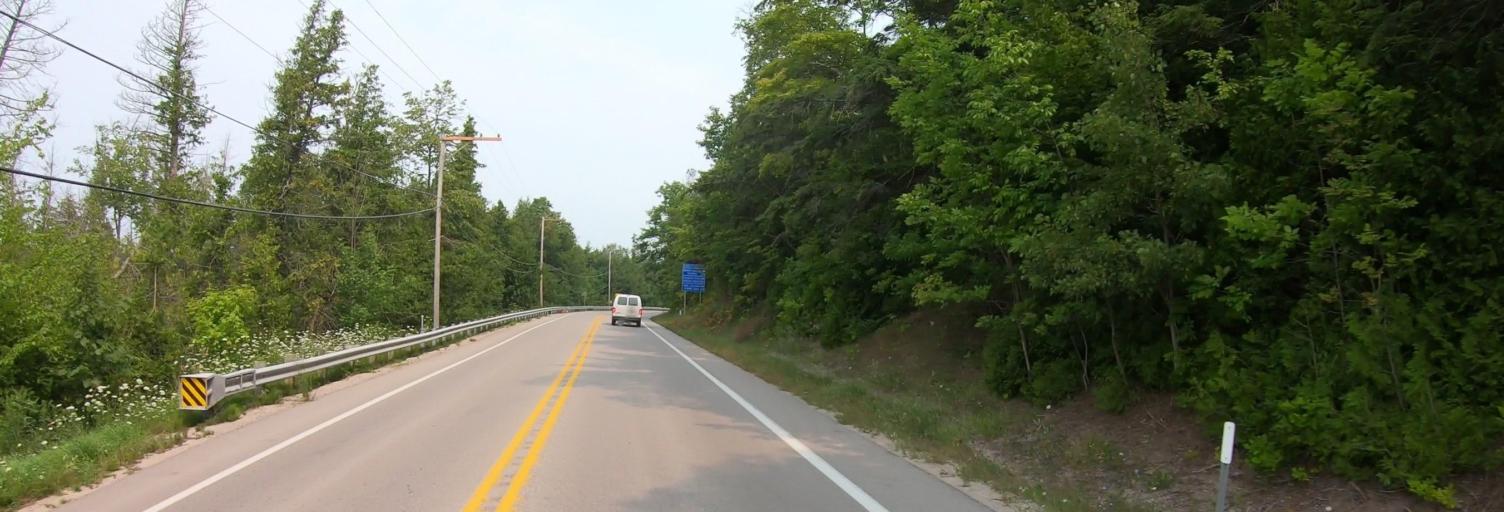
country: US
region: Michigan
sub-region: Leelanau County
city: Leland
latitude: 44.9915
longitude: -85.7702
